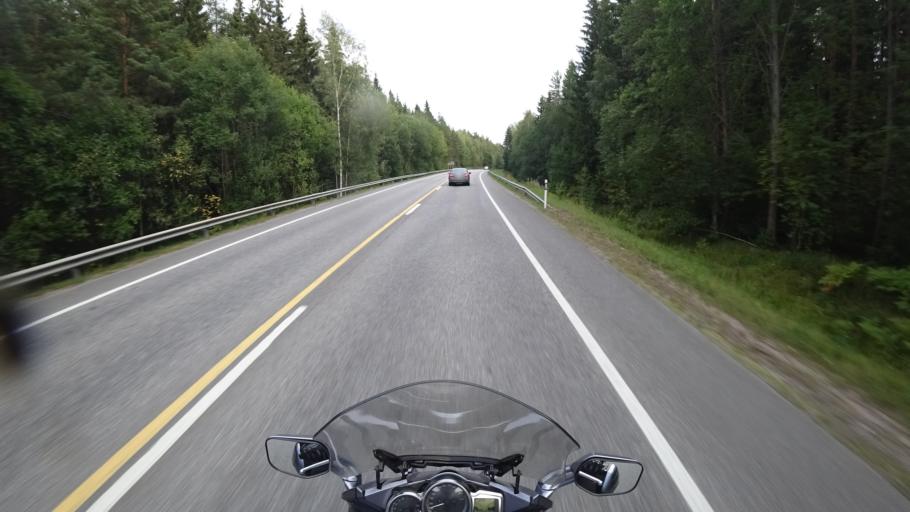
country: FI
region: Uusimaa
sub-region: Raaseporin
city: Karis
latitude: 60.0868
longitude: 23.6538
